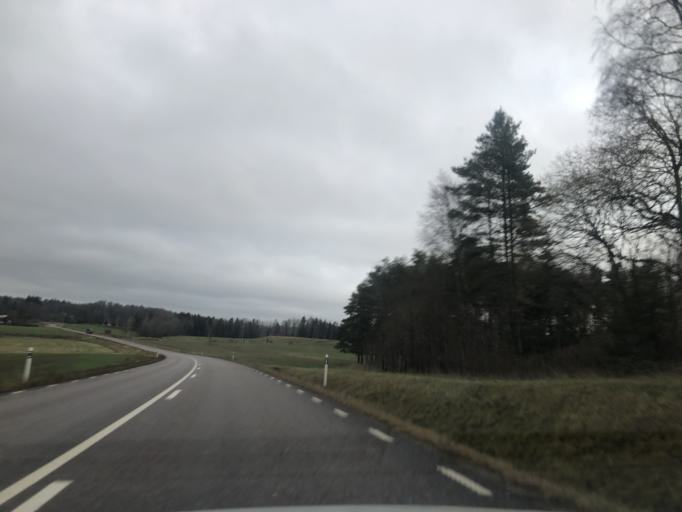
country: SE
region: Vaestra Goetaland
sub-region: Ulricehamns Kommun
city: Ulricehamn
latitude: 57.8755
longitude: 13.4343
